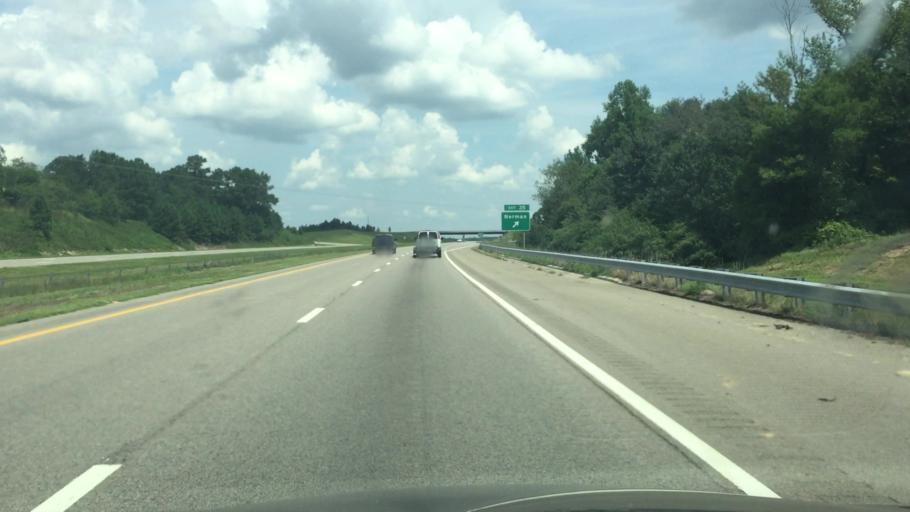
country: US
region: North Carolina
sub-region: Richmond County
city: Ellerbe
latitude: 35.1674
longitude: -79.7155
